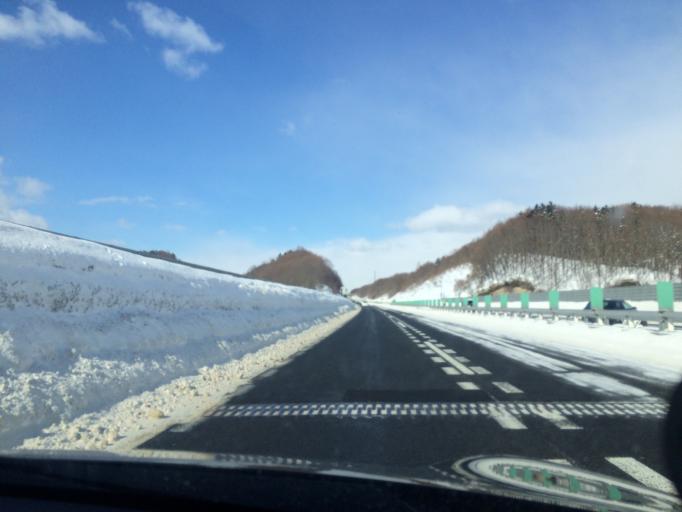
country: JP
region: Hokkaido
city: Kitahiroshima
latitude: 42.9233
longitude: 141.5414
